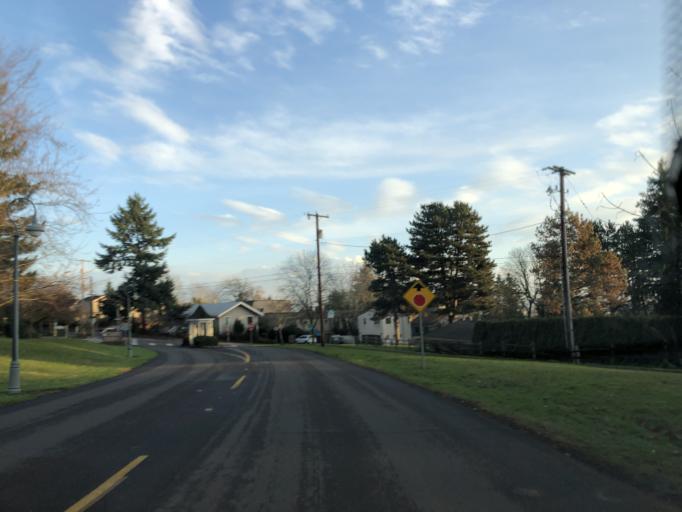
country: US
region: Washington
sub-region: Clark County
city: Vancouver
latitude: 45.6264
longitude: -122.6549
